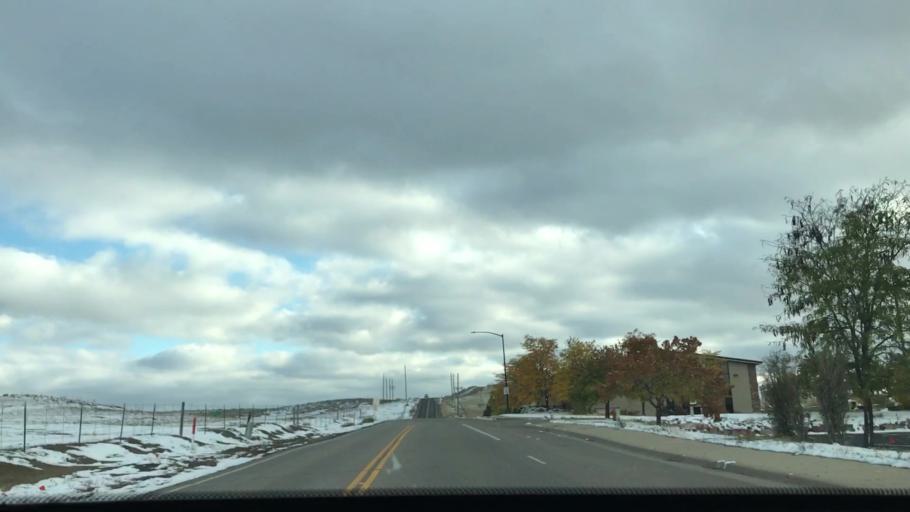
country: US
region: Colorado
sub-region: Boulder County
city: Lafayette
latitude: 39.9738
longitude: -105.0719
